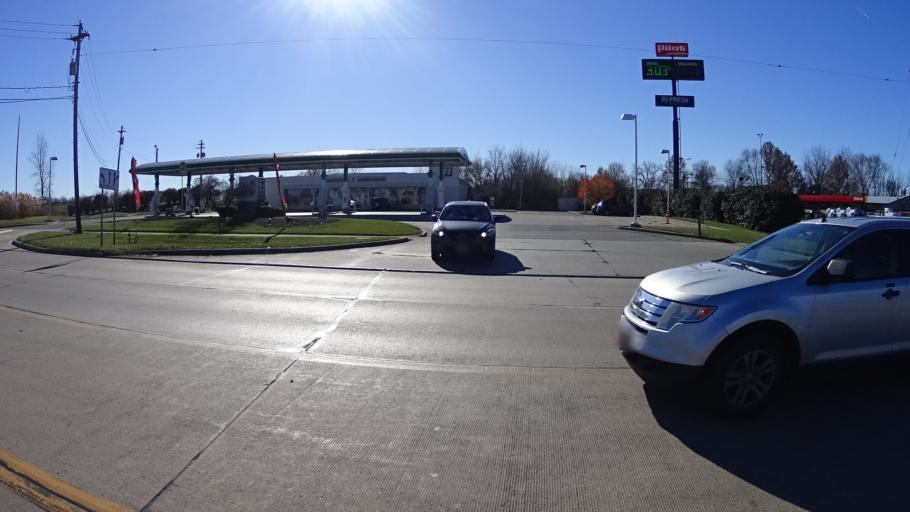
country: US
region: Ohio
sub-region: Lorain County
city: Avon
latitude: 41.4653
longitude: -82.0592
